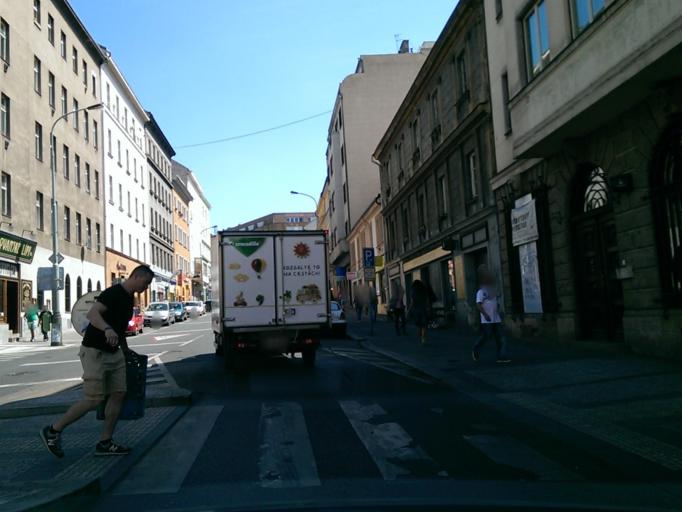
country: CZ
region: Praha
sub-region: Praha 8
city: Karlin
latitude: 50.0874
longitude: 14.4530
